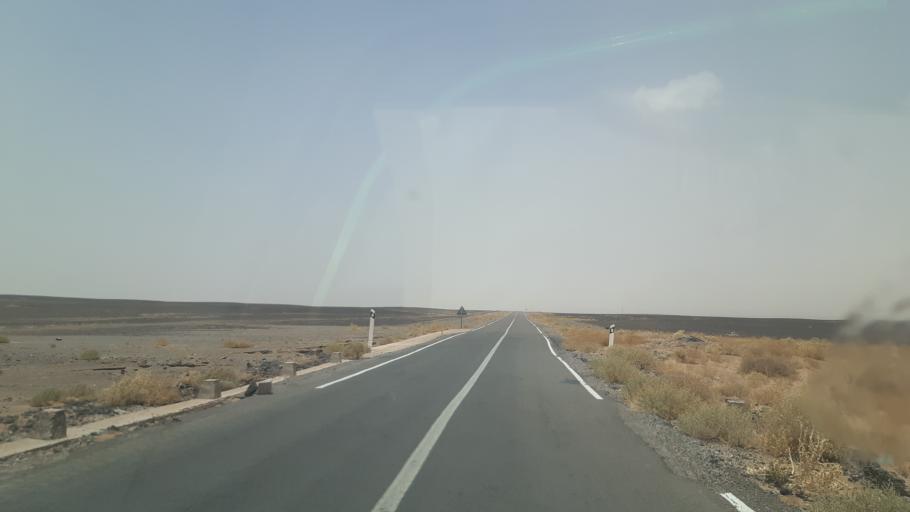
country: MA
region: Meknes-Tafilalet
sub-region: Errachidia
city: Jorf
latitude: 31.1783
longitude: -4.0854
